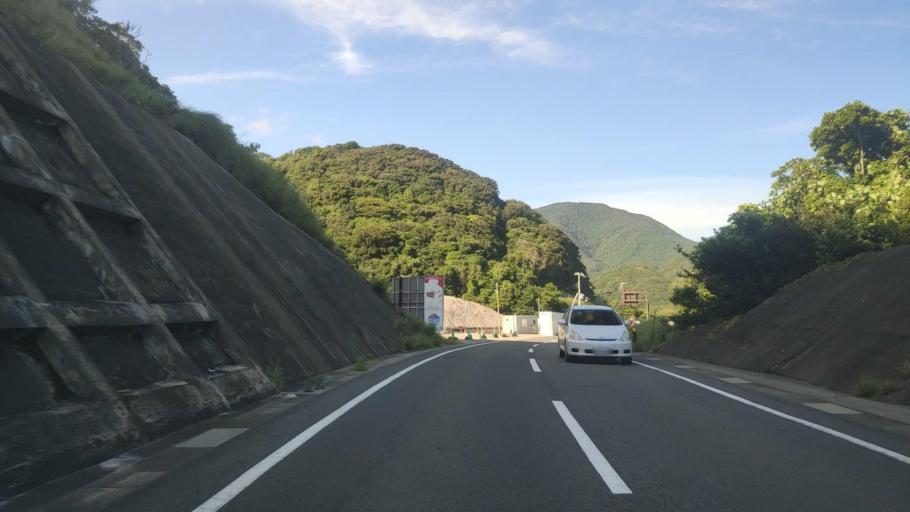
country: JP
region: Wakayama
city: Tanabe
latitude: 33.5084
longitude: 135.6008
